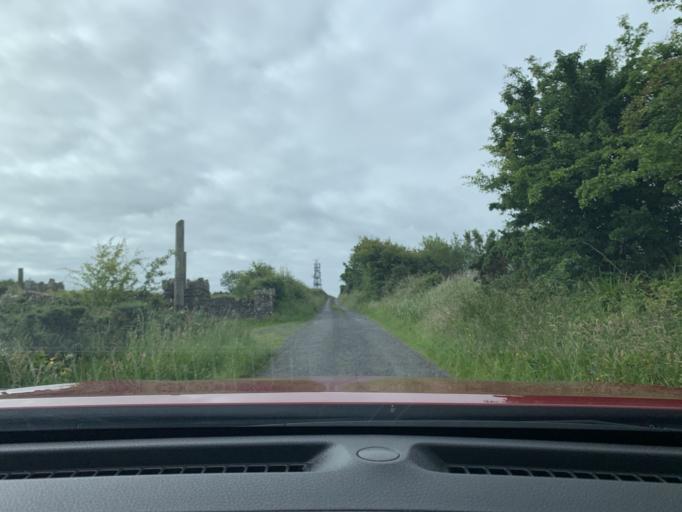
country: IE
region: Connaught
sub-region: Sligo
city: Sligo
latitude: 54.3719
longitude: -8.5207
